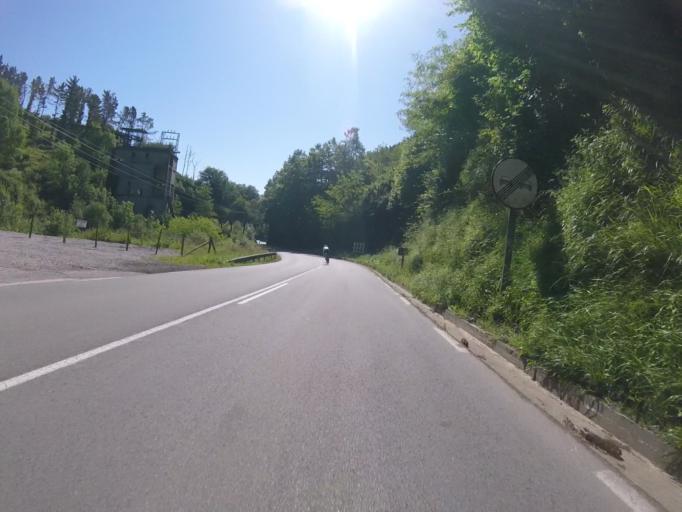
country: ES
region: Basque Country
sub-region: Provincia de Guipuzcoa
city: Alegria de Oria
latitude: 43.1232
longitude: -2.1074
